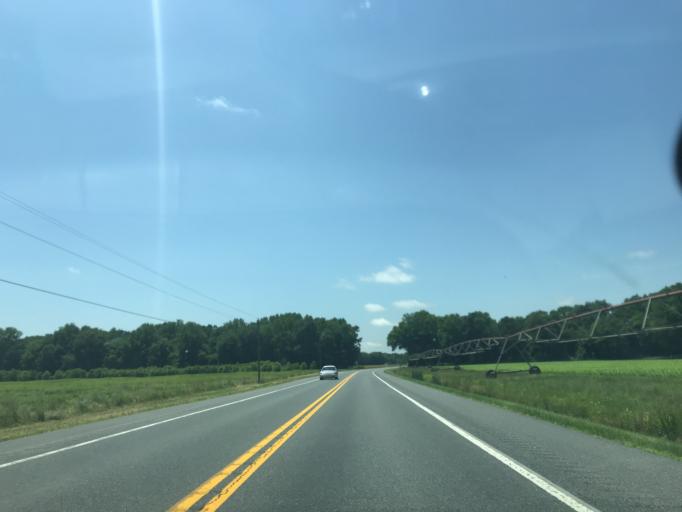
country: US
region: Maryland
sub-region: Caroline County
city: Federalsburg
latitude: 38.6305
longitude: -75.7219
